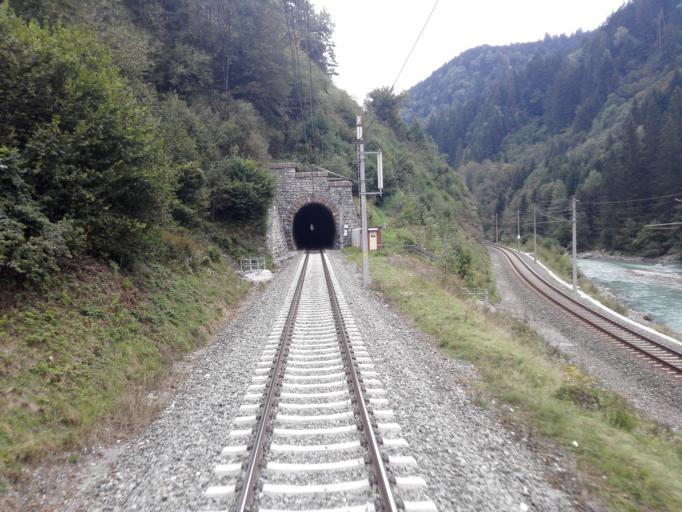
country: AT
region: Salzburg
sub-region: Politischer Bezirk Zell am See
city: Taxenbach
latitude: 47.2954
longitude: 12.9848
